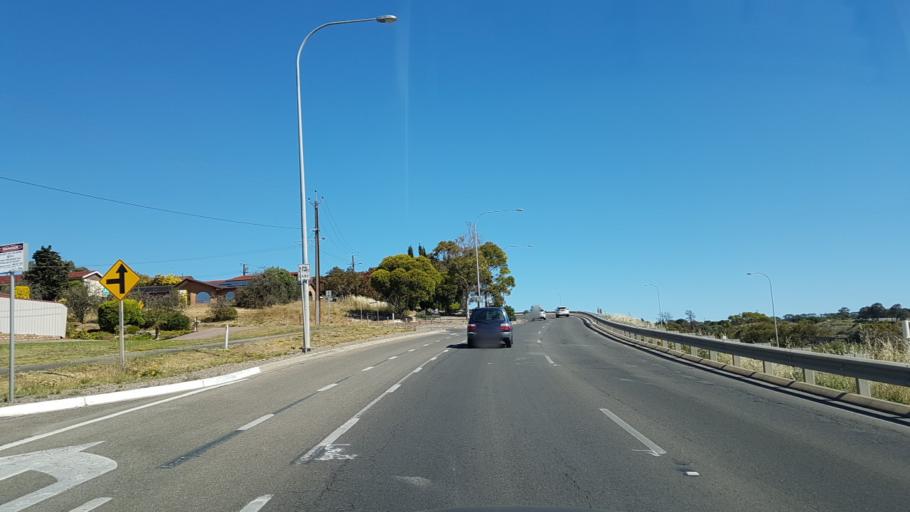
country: AU
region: South Australia
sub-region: Onkaparinga
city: Bedford Park
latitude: -35.0342
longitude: 138.5634
